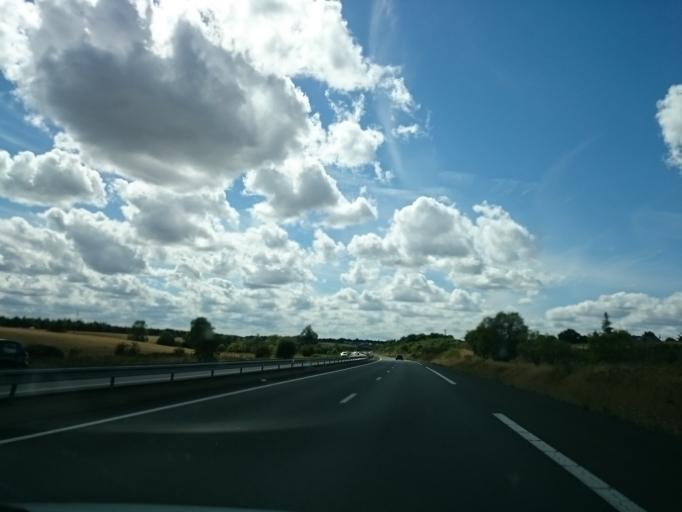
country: FR
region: Pays de la Loire
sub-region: Departement de Maine-et-Loire
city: Ingrandes
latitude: 47.4267
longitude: -0.9330
